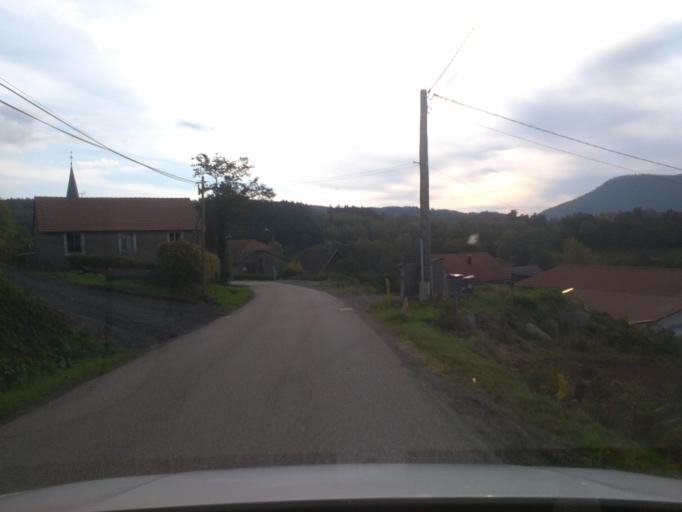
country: FR
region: Lorraine
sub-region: Departement des Vosges
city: Senones
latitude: 48.3437
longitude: 7.0101
